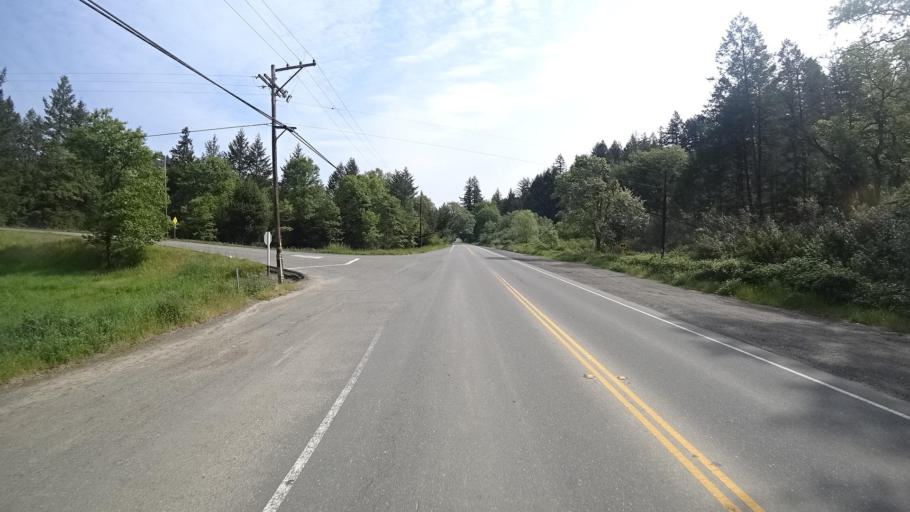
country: US
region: California
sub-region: Humboldt County
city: Redway
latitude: 40.1386
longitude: -123.8132
